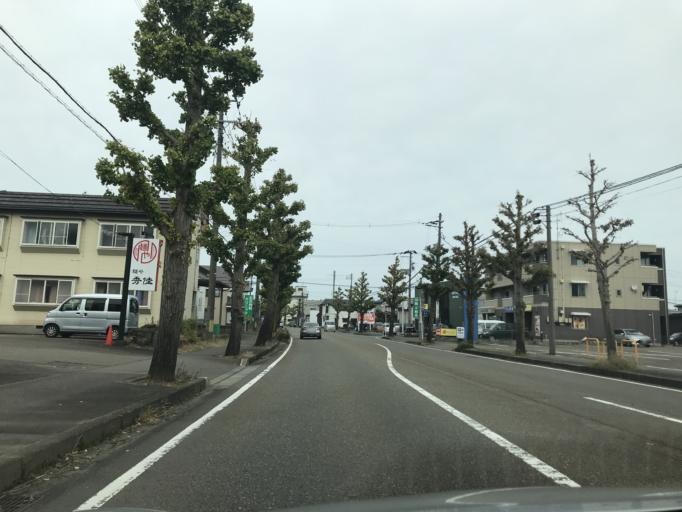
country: JP
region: Niigata
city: Nagaoka
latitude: 37.4283
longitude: 138.8365
